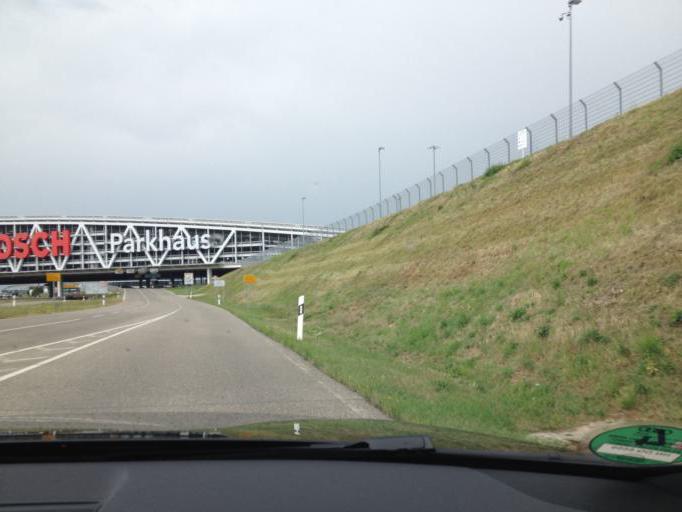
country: DE
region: Baden-Wuerttemberg
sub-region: Regierungsbezirk Stuttgart
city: Leinfelden-Echterdingen
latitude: 48.6962
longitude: 9.1902
